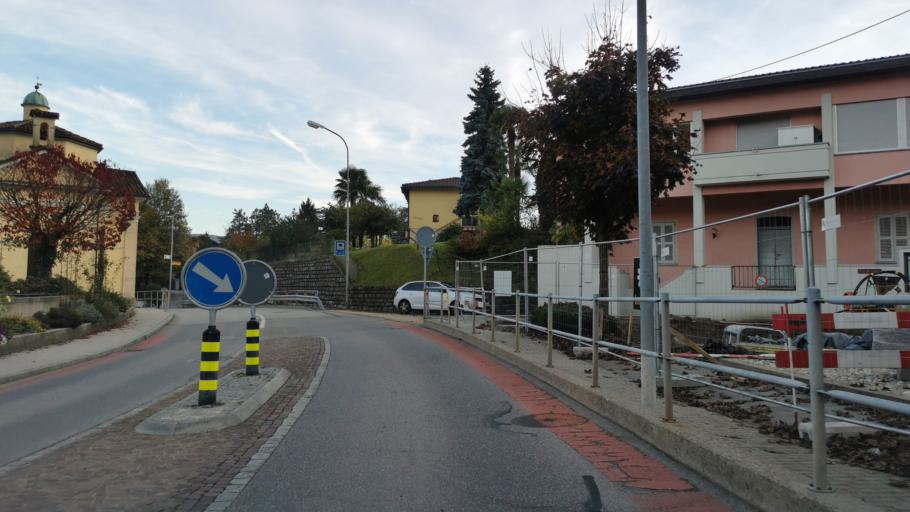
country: CH
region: Ticino
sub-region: Lugano District
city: Pura
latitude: 45.9844
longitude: 8.8699
